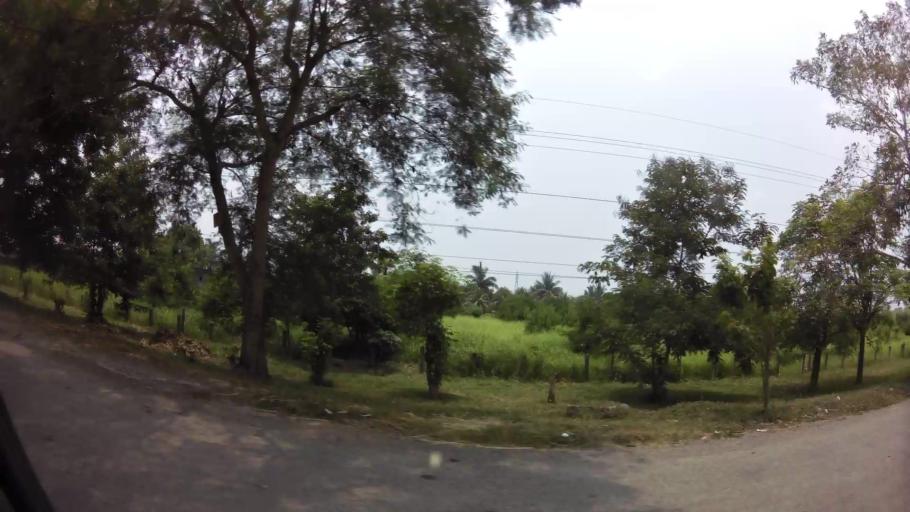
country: HN
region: Yoro
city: El Progreso
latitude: 15.4055
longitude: -87.8250
